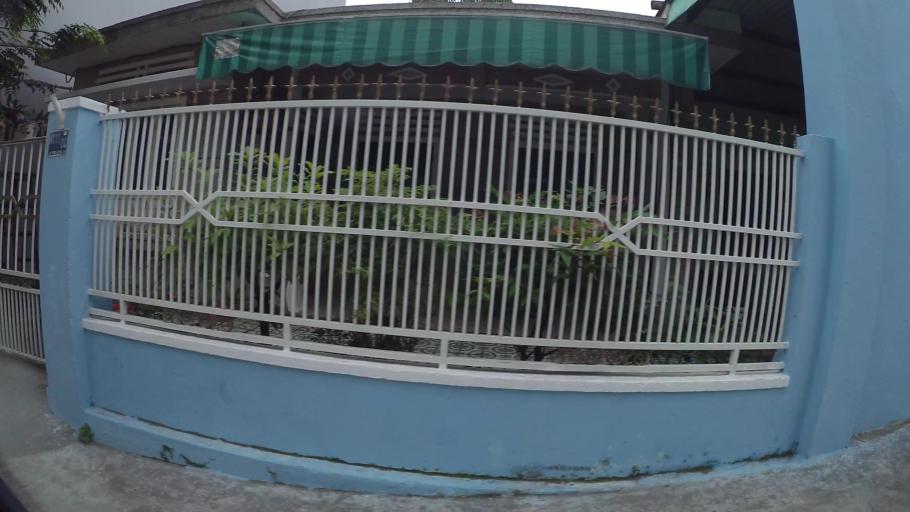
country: VN
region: Da Nang
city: Cam Le
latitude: 16.0282
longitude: 108.2240
